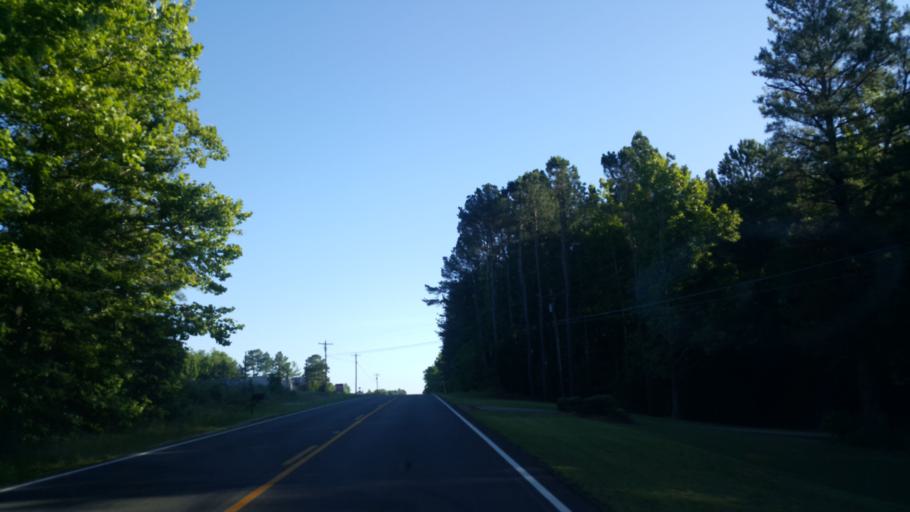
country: US
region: Tennessee
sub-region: Henderson County
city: Lexington
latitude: 35.5500
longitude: -88.3847
